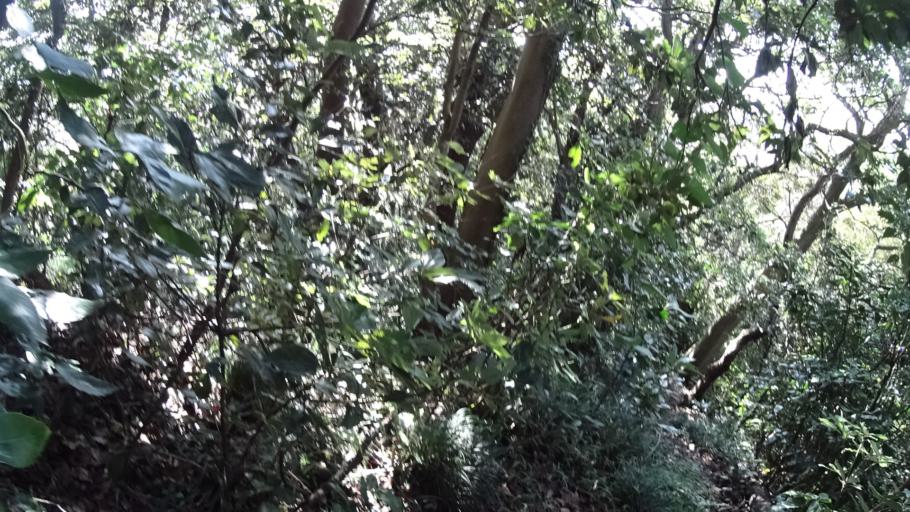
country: JP
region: Kanagawa
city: Hayama
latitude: 35.2767
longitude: 139.6172
